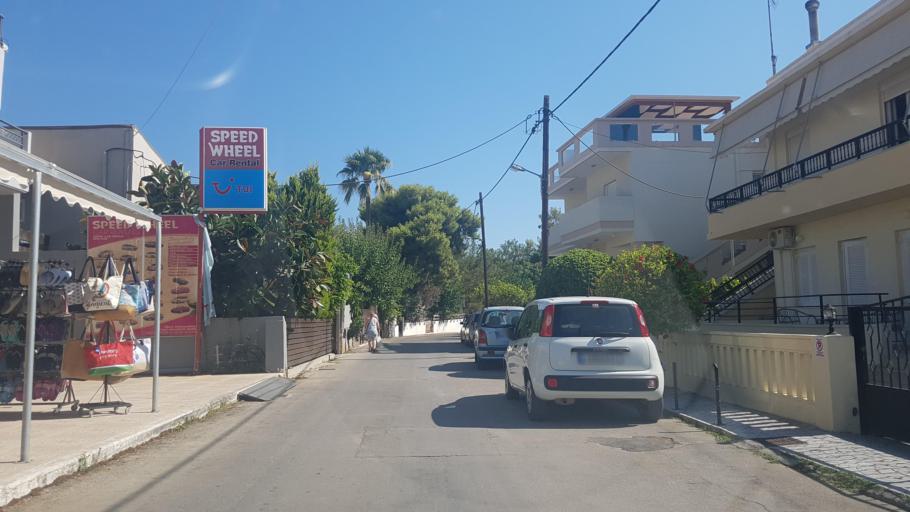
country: GR
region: Crete
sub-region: Nomos Chanias
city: Daratsos
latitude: 35.5116
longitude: 23.9797
